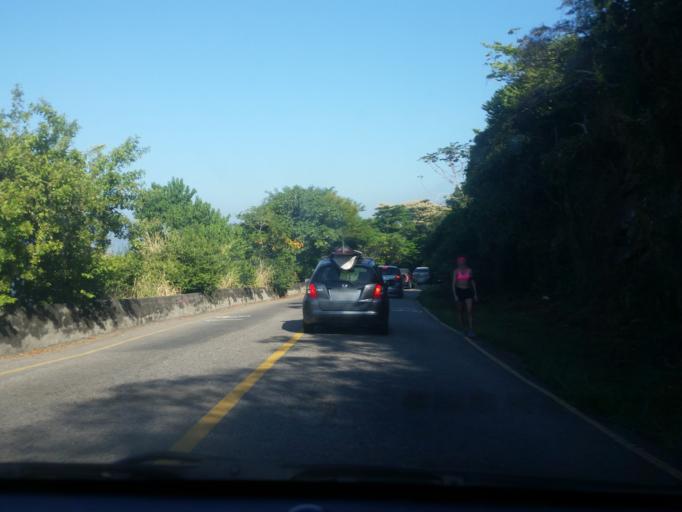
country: BR
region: Rio de Janeiro
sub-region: Nilopolis
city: Nilopolis
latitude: -23.0472
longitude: -43.5104
